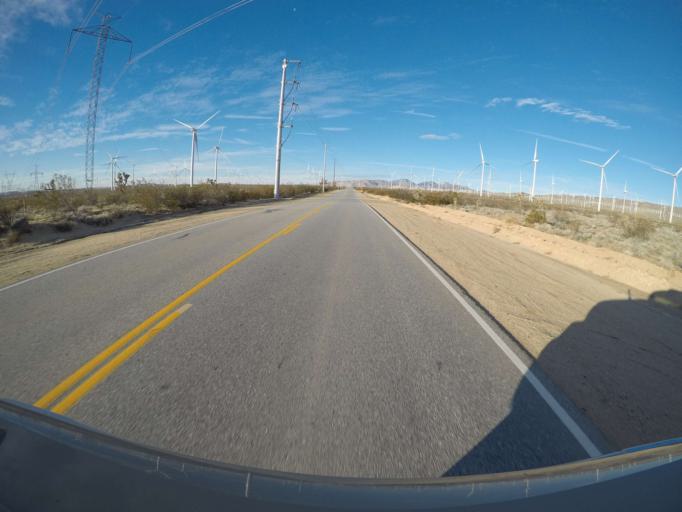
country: US
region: California
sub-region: Kern County
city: Mojave
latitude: 35.0487
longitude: -118.2094
